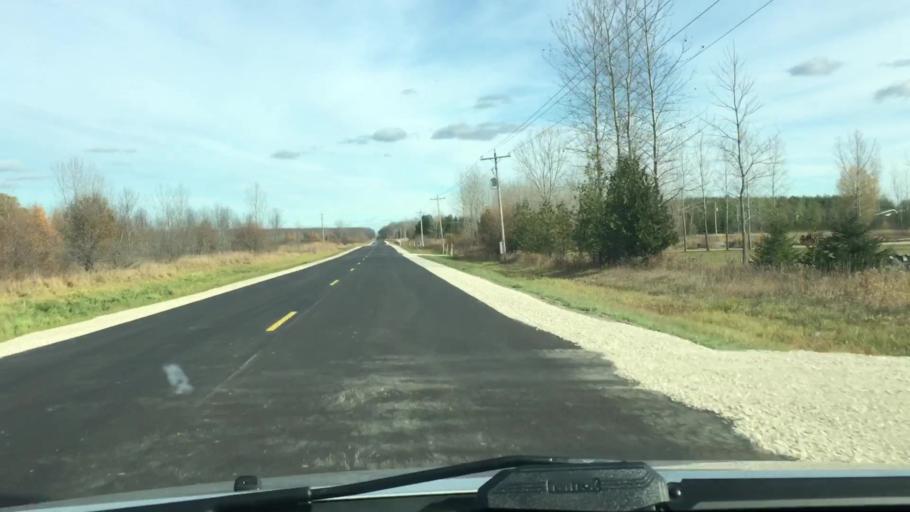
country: US
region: Wisconsin
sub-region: Kewaunee County
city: Algoma
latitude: 44.6901
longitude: -87.5492
